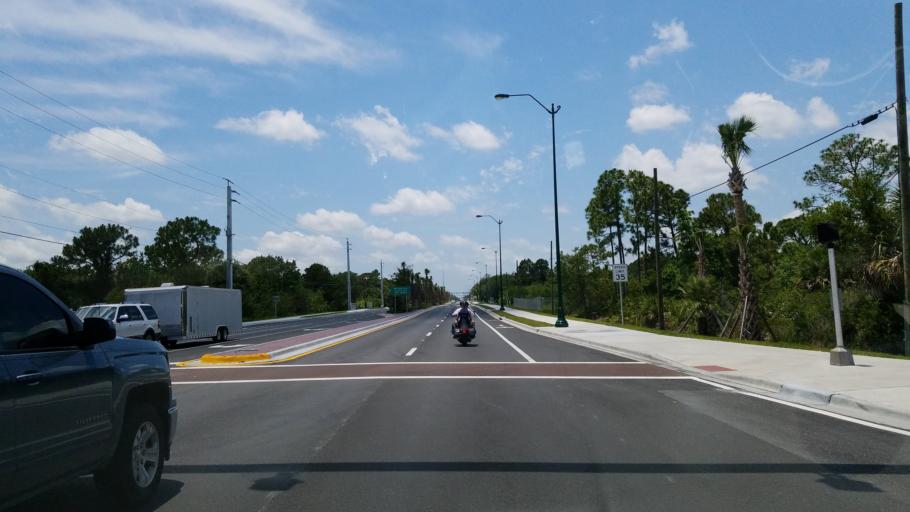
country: US
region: Florida
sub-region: Martin County
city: Palm City
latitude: 27.1612
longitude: -80.2766
